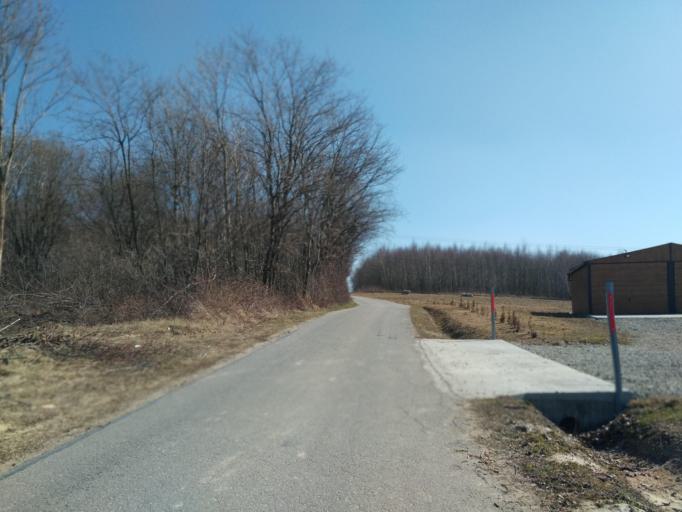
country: PL
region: Subcarpathian Voivodeship
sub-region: Powiat rzeszowski
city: Zglobien
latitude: 49.9849
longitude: 21.8309
